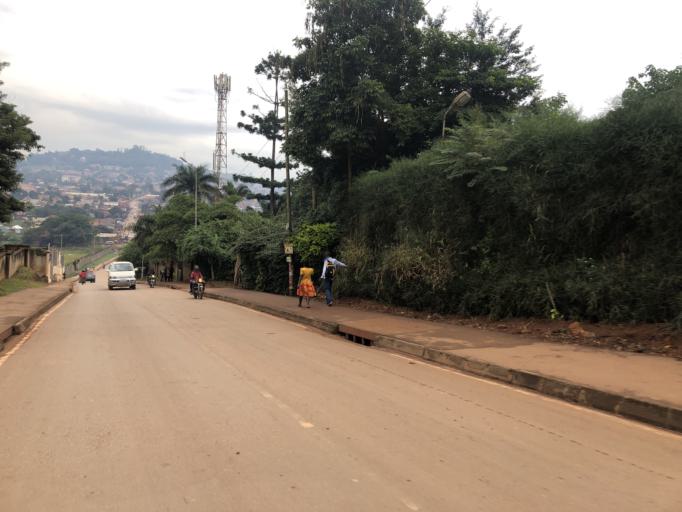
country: UG
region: Central Region
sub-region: Kampala District
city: Kampala
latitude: 0.2854
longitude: 32.6061
